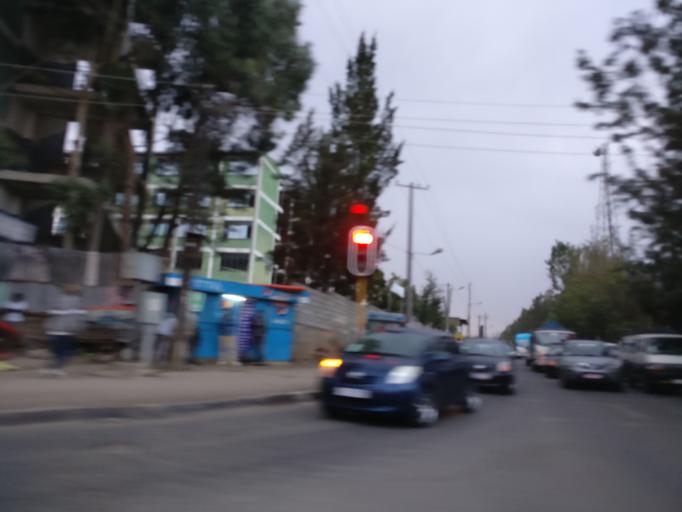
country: ET
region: Adis Abeba
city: Addis Ababa
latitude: 9.0167
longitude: 38.7460
